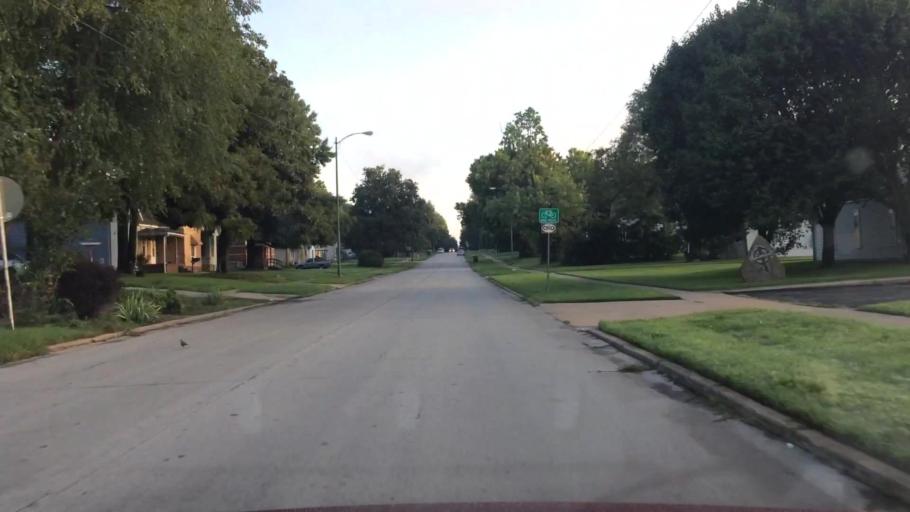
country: US
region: Missouri
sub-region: Greene County
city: Springfield
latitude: 37.2187
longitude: -93.2810
